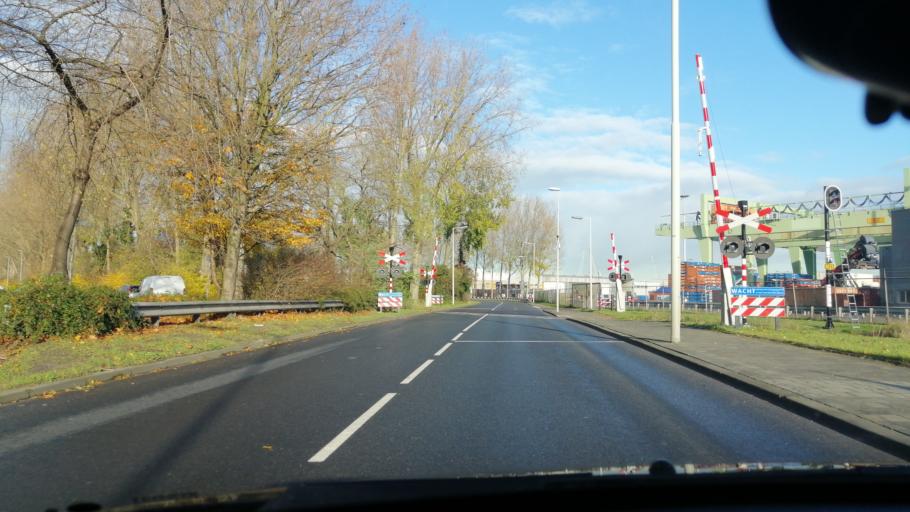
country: NL
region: South Holland
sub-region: Gemeente Rotterdam
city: Delfshaven
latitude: 51.8900
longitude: 4.4255
